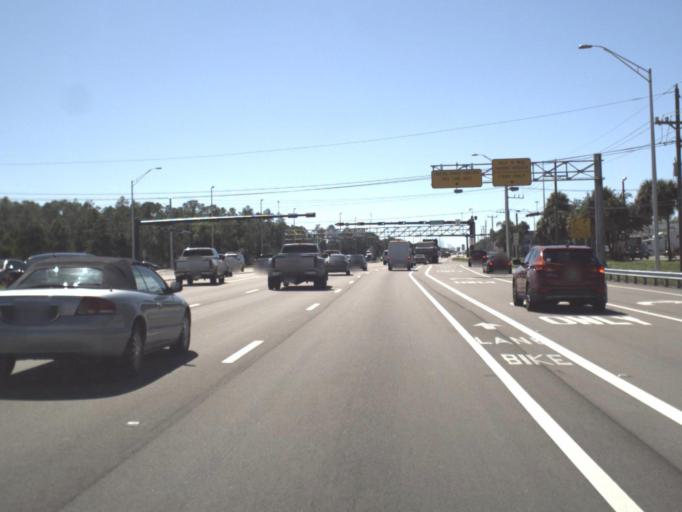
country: US
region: Florida
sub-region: Collier County
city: Golden Gate
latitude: 26.1562
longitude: -81.6867
